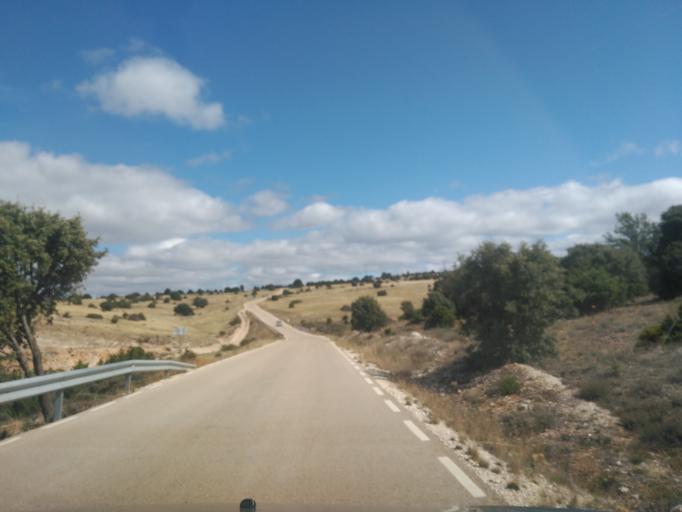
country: ES
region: Castille and Leon
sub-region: Provincia de Soria
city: Espejon
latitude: 41.8338
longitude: -3.2483
